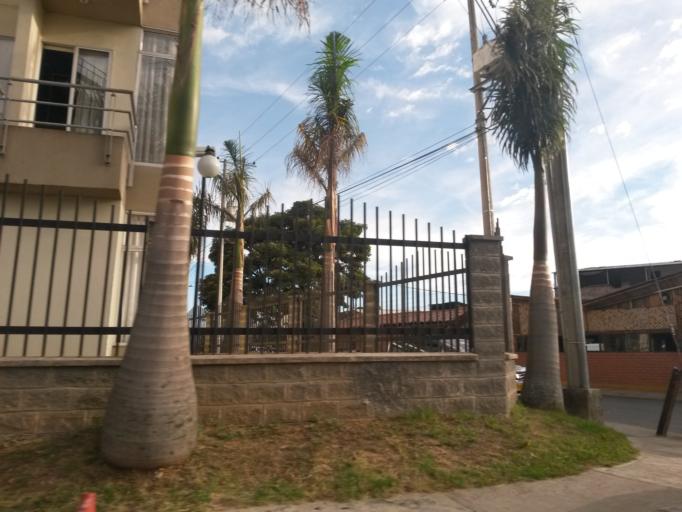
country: CO
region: Cauca
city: Popayan
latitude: 2.4487
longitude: -76.6084
